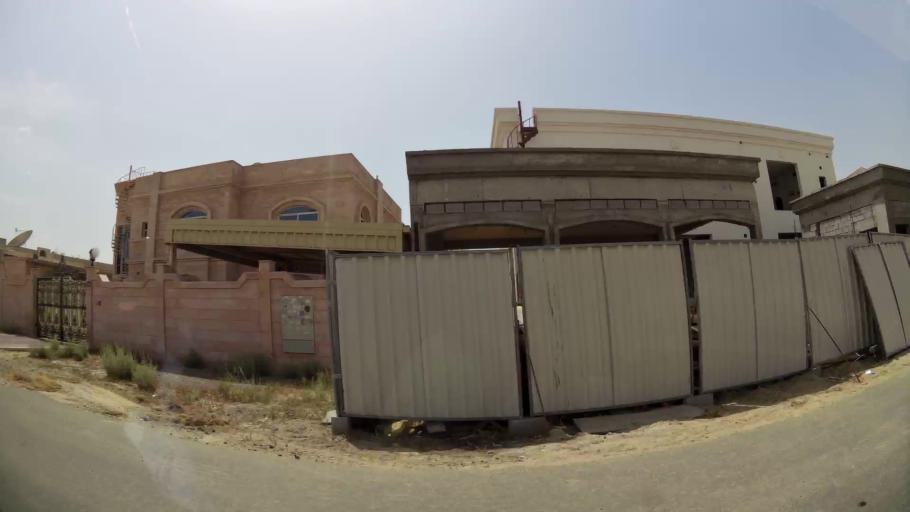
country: AE
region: Ash Shariqah
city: Sharjah
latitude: 25.2453
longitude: 55.4312
